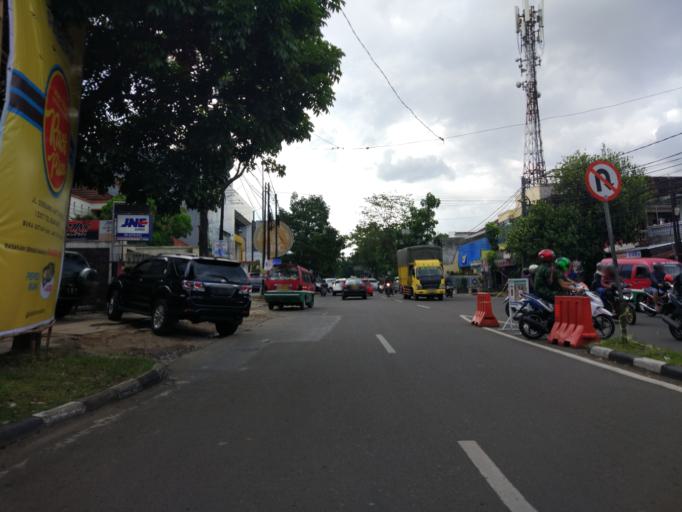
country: ID
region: West Java
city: Bandung
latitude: -6.9246
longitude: 107.6275
